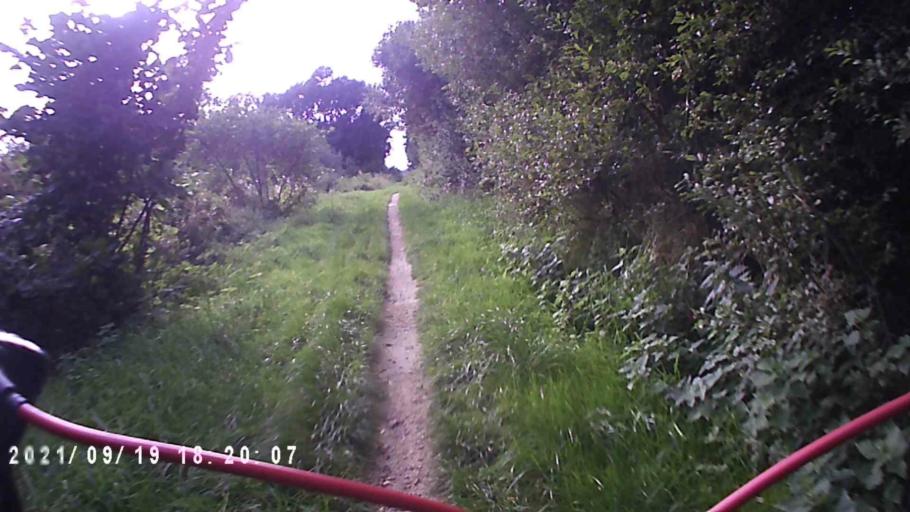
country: NL
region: Groningen
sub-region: Gemeente Appingedam
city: Appingedam
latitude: 53.2703
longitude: 6.8714
